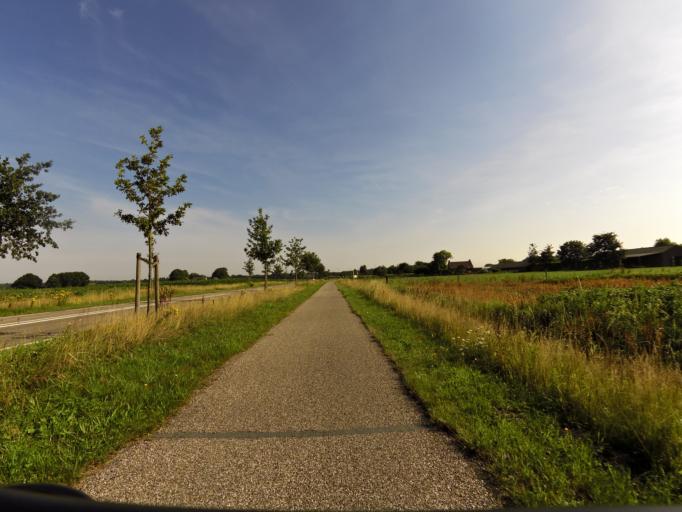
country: NL
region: North Brabant
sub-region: Gemeente Woensdrecht
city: Woensdrecht
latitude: 51.4452
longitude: 4.3789
